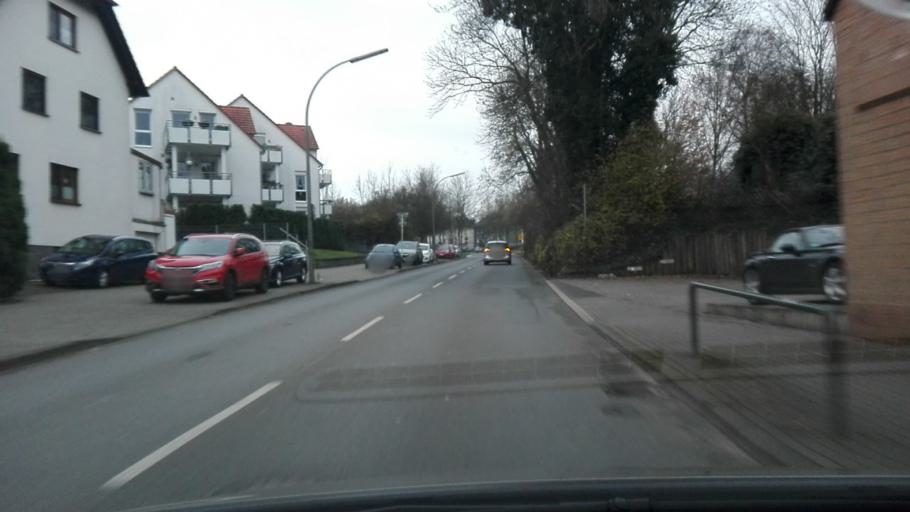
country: DE
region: North Rhine-Westphalia
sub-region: Regierungsbezirk Arnsberg
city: Dortmund
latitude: 51.5202
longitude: 7.5198
